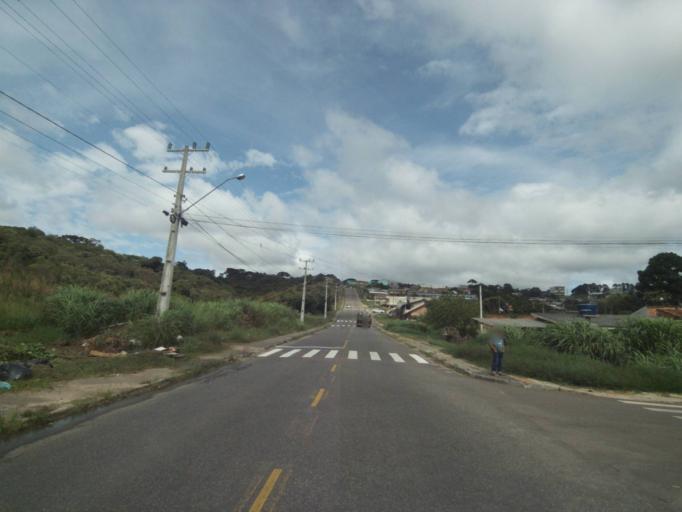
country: BR
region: Parana
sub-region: Quatro Barras
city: Quatro Barras
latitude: -25.3464
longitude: -49.0790
